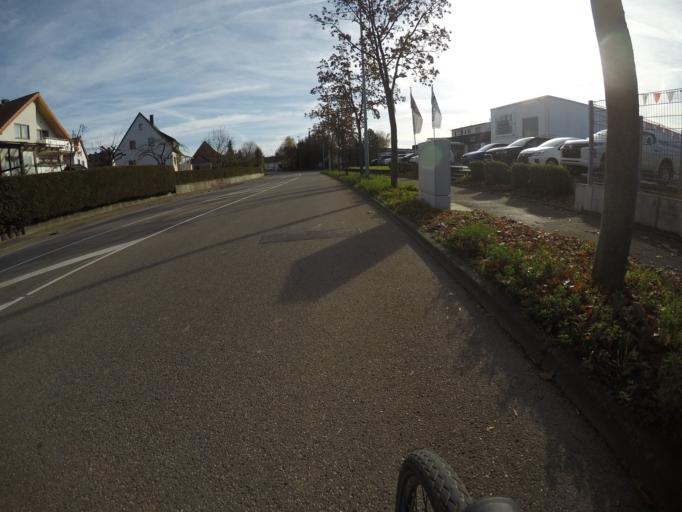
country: DE
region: Baden-Wuerttemberg
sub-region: Regierungsbezirk Stuttgart
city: Weinstadt-Endersbach
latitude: 48.8214
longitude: 9.3443
